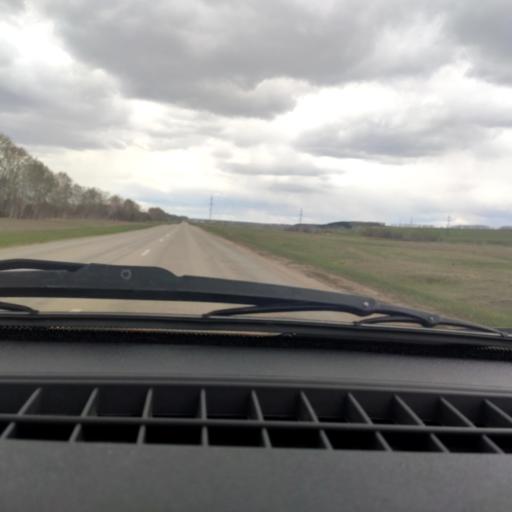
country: RU
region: Bashkortostan
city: Chekmagush
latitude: 55.1217
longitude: 54.7319
